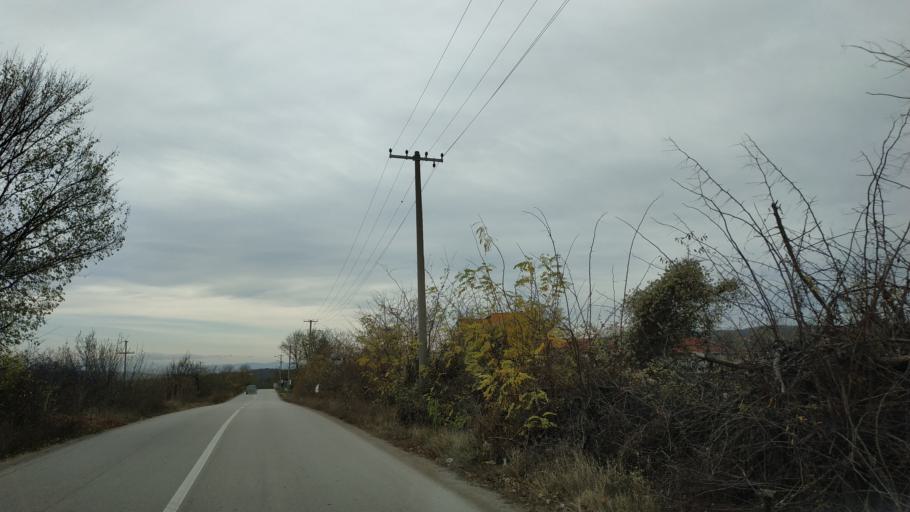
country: RS
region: Central Serbia
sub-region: Nisavski Okrug
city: Nis
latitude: 43.3558
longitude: 21.9484
